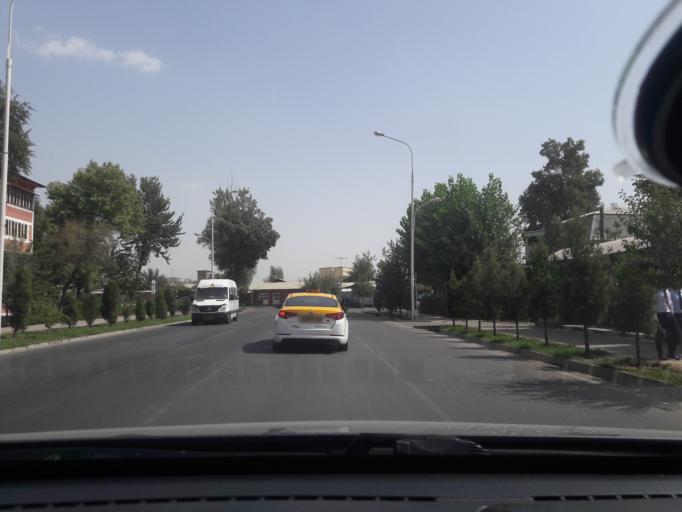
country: TJ
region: Dushanbe
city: Dushanbe
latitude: 38.5641
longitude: 68.7613
